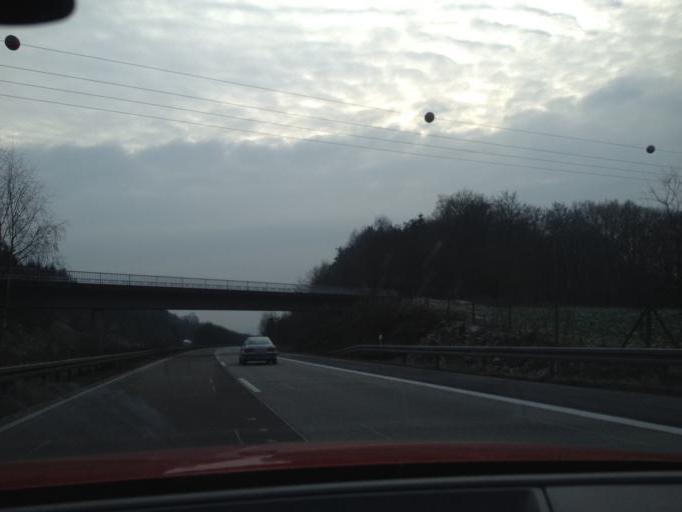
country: DE
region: Hesse
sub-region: Regierungsbezirk Darmstadt
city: Ranstadt
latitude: 50.3640
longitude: 8.9380
